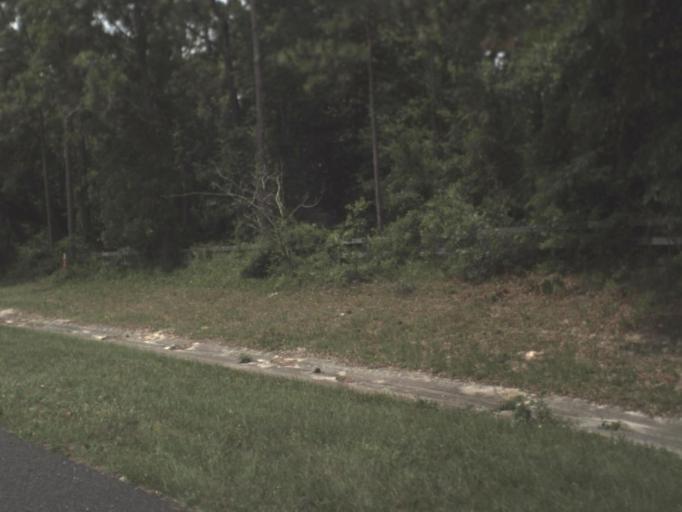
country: US
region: Florida
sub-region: Clay County
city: Green Cove Springs
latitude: 29.8759
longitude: -81.6643
